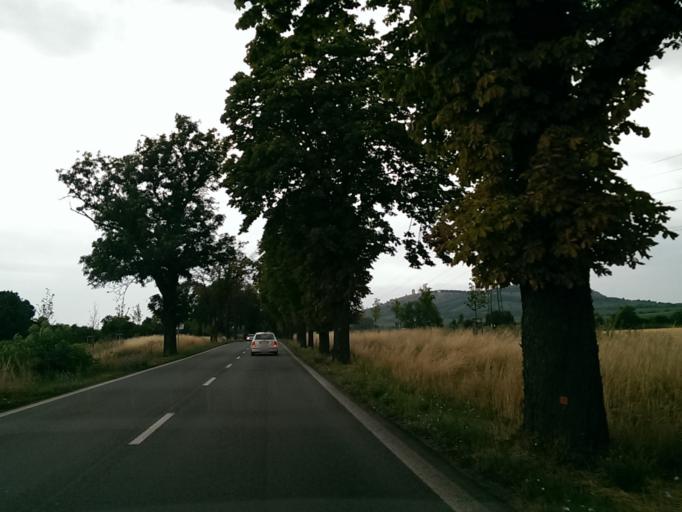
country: CZ
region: South Moravian
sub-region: Okres Breclav
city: Mikulov
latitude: 48.7918
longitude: 16.6714
